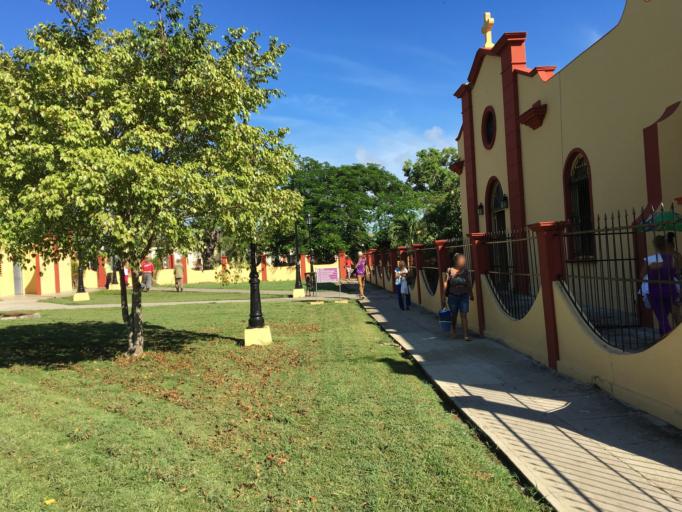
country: CU
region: La Habana
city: Santiago de las Vegas
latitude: 22.9510
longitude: -82.4224
